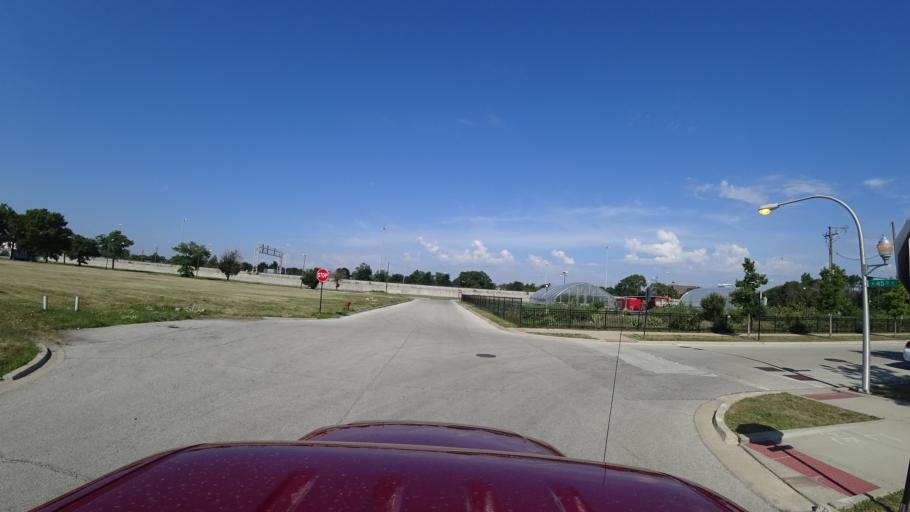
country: US
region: Illinois
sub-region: Cook County
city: Chicago
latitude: 41.8131
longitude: -87.6271
